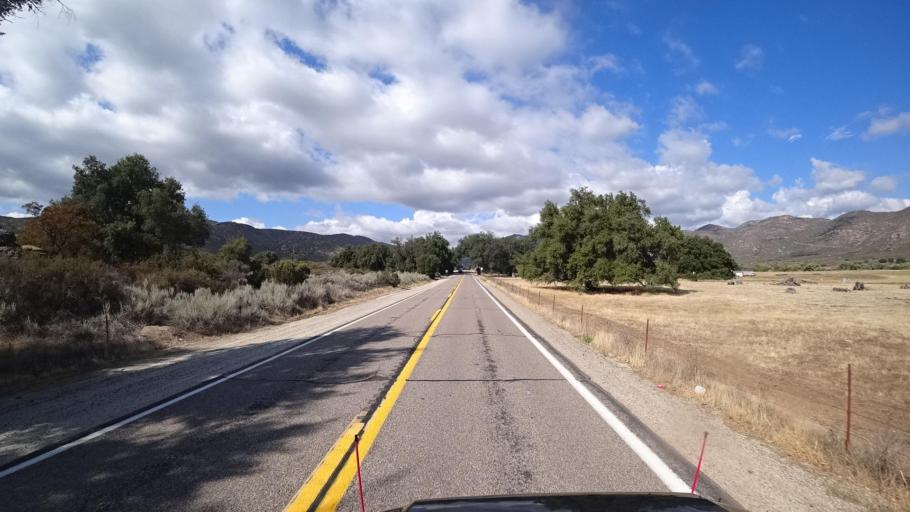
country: US
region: California
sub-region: San Diego County
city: Pine Valley
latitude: 32.7449
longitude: -116.4941
